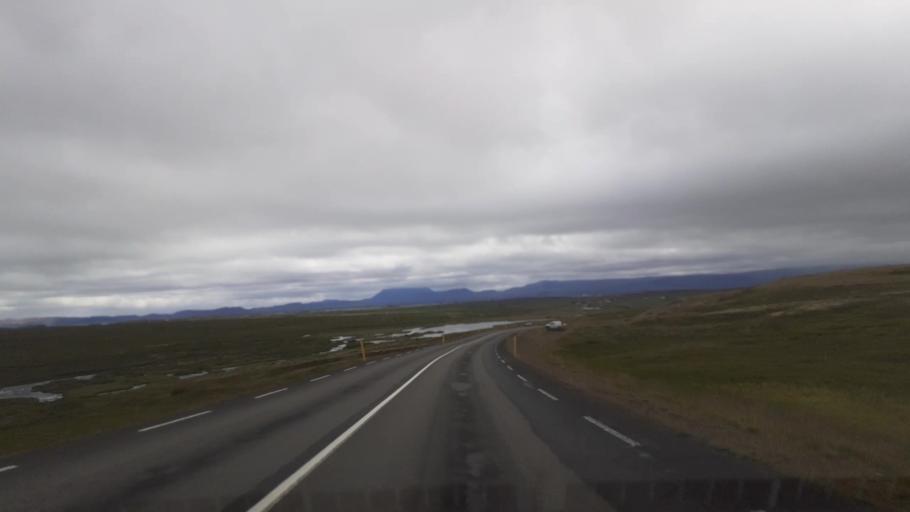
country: IS
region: Northeast
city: Laugar
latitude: 65.5957
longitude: -17.1838
